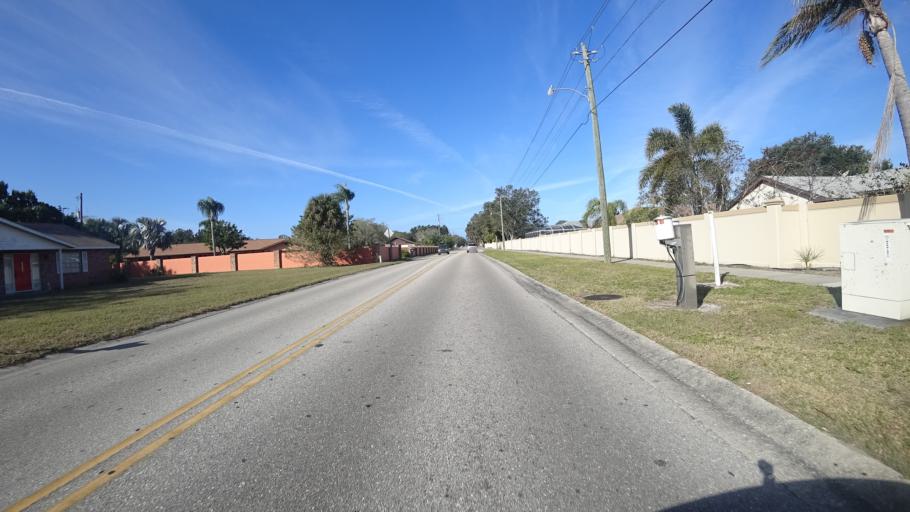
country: US
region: Florida
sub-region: Manatee County
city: West Bradenton
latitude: 27.4812
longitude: -82.6133
